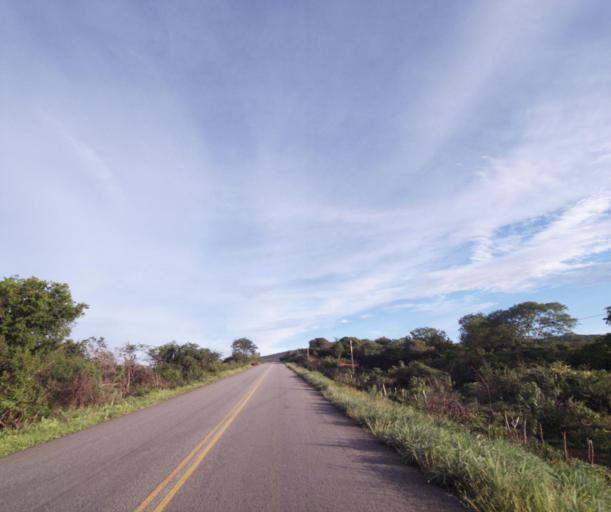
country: BR
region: Bahia
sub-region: Caetite
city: Caetite
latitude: -14.1799
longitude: -42.1675
